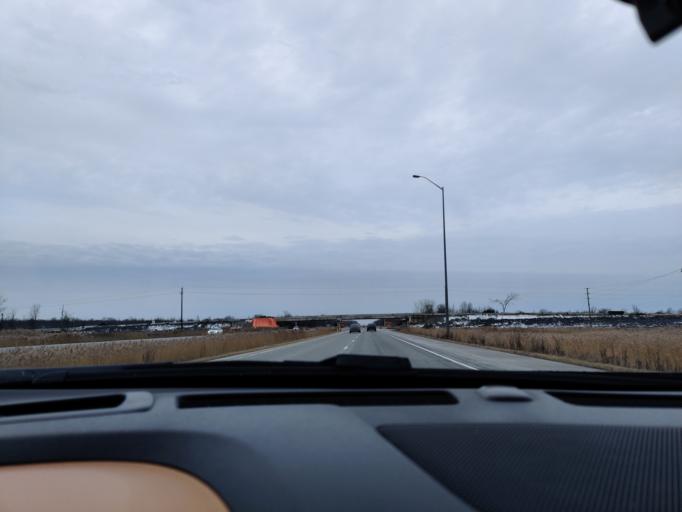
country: US
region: New York
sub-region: St. Lawrence County
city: Norfolk
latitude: 44.9184
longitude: -75.1947
